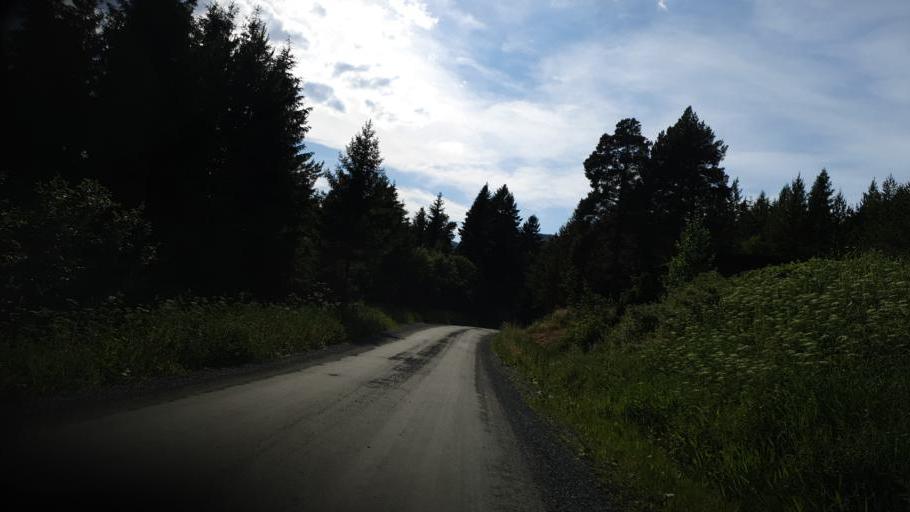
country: NO
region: Sor-Trondelag
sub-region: Trondheim
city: Trondheim
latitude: 63.5755
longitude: 10.3848
